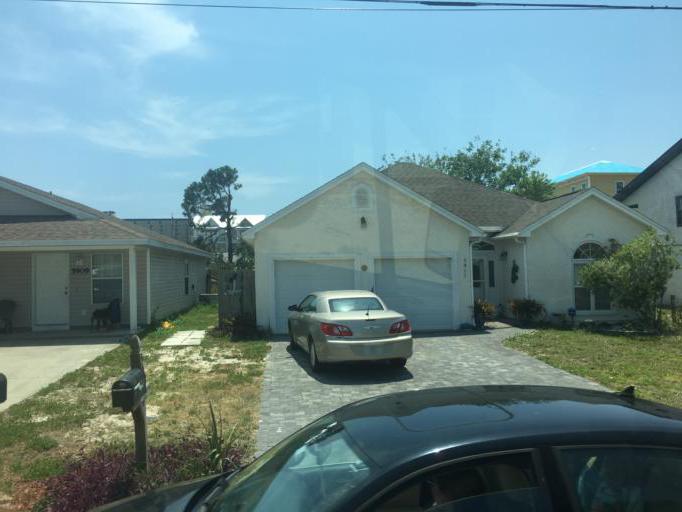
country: US
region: Florida
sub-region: Bay County
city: Lower Grand Lagoon
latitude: 30.1498
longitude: -85.7594
